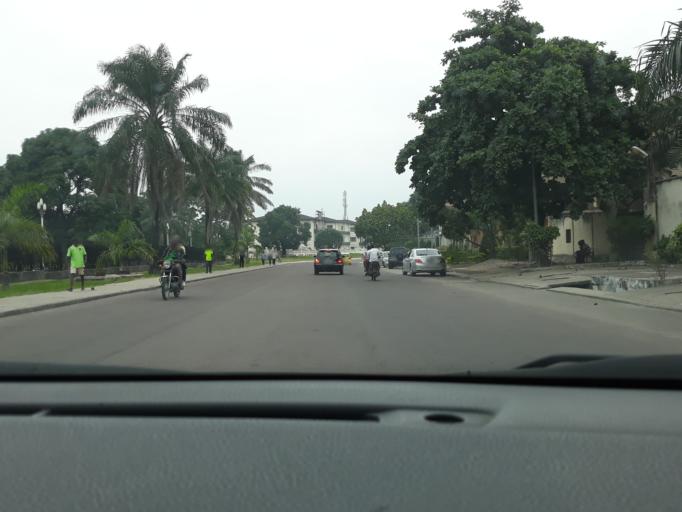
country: CD
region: Kinshasa
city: Kinshasa
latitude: -4.3310
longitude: 15.3016
